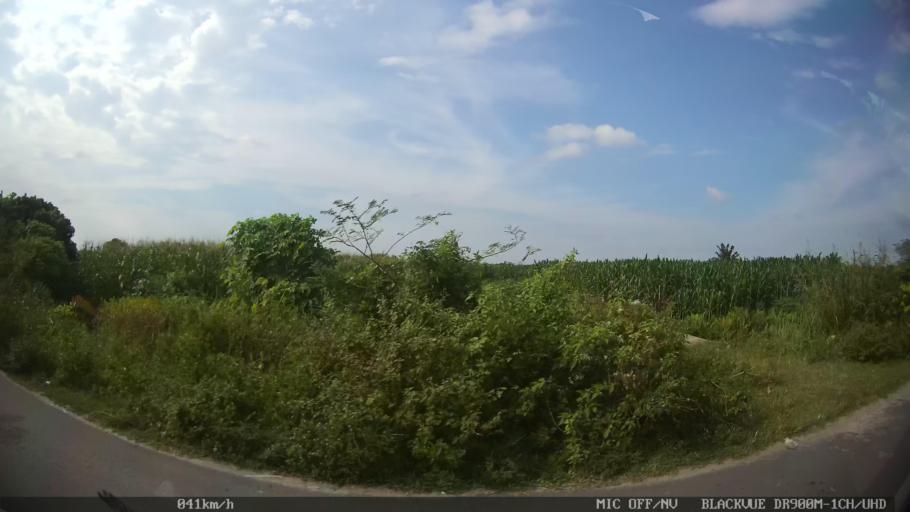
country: ID
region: North Sumatra
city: Medan
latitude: 3.5731
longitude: 98.7657
